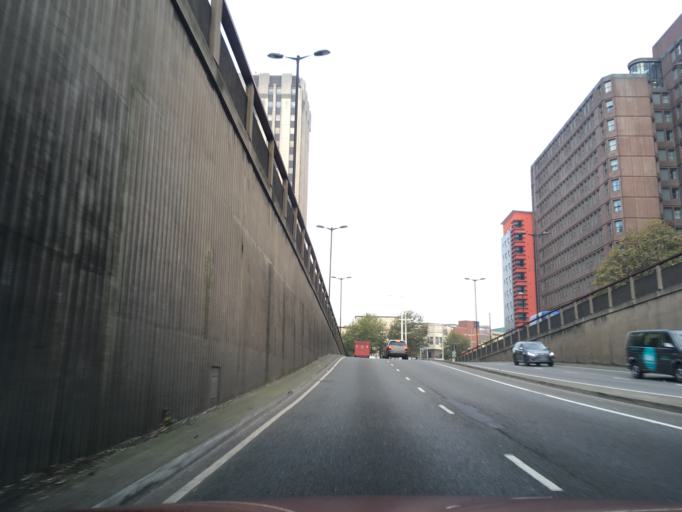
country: GB
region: England
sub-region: Bristol
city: Bristol
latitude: 51.4559
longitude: -2.5839
